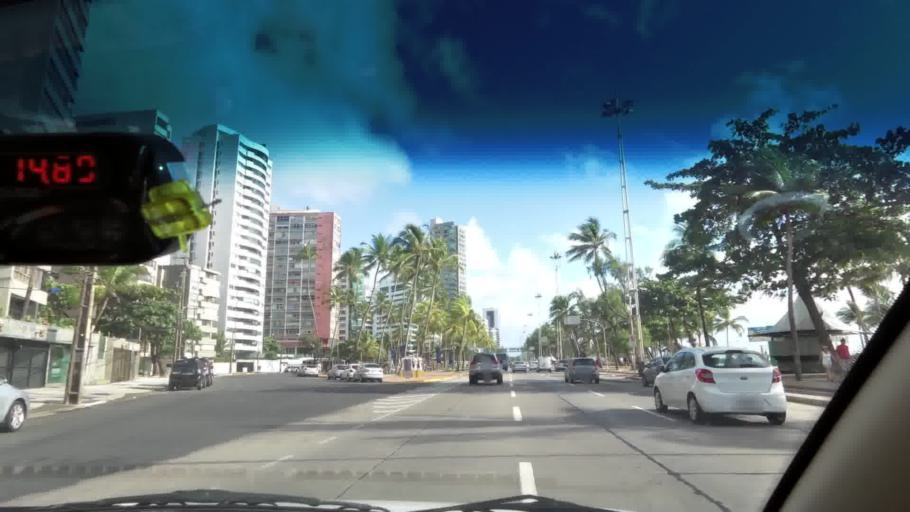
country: BR
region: Pernambuco
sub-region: Recife
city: Recife
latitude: -8.1063
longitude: -34.8875
